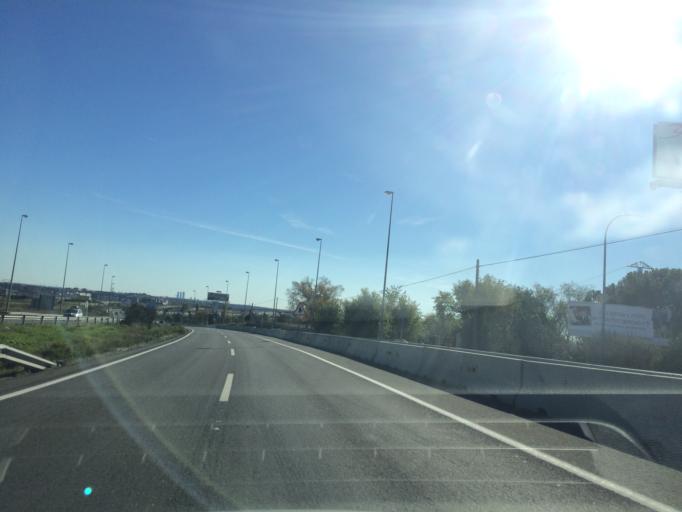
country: ES
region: Madrid
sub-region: Provincia de Madrid
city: Colmenar Viejo
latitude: 40.6394
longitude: -3.7315
